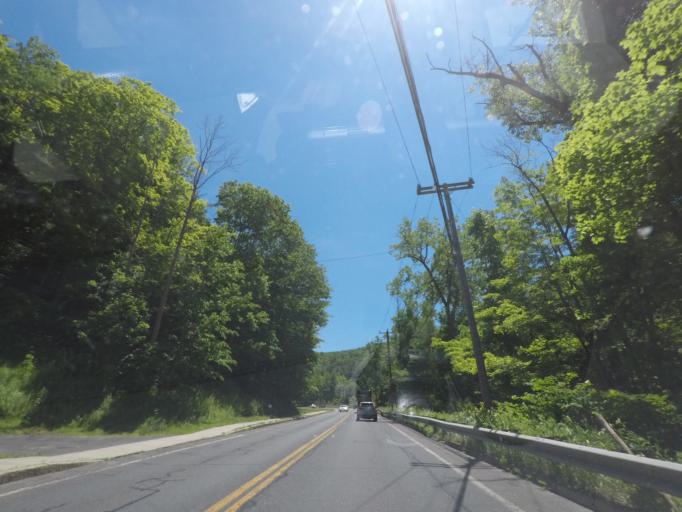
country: US
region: Massachusetts
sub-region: Berkshire County
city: Lee
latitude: 42.2960
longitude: -73.2305
